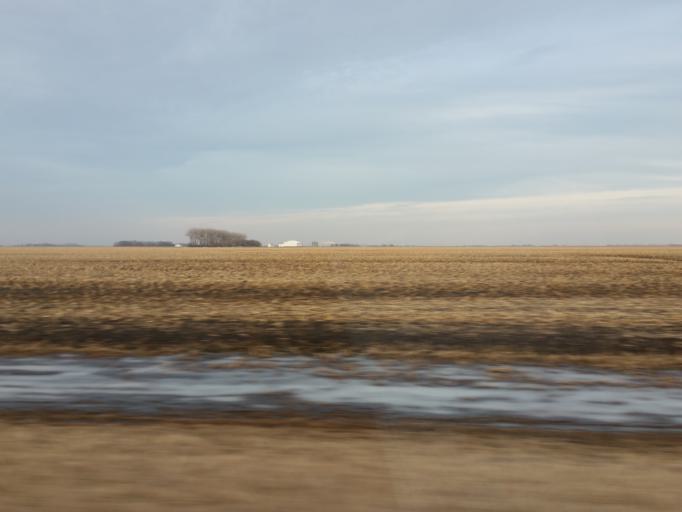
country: US
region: North Dakota
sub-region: Traill County
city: Mayville
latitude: 47.4168
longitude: -97.3261
